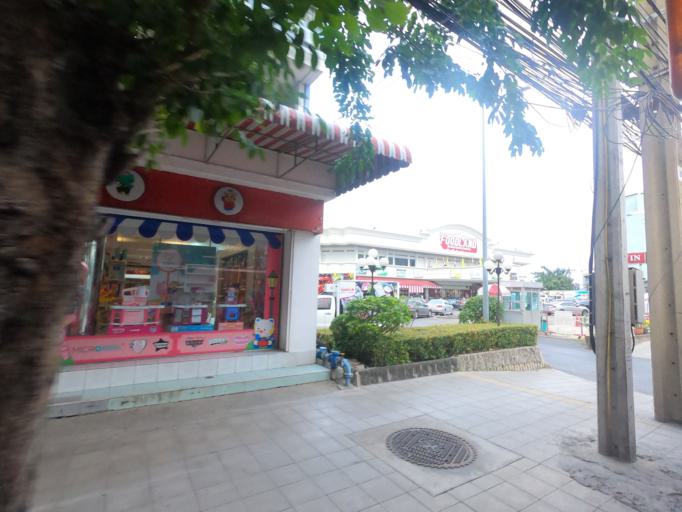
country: TH
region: Bangkok
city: Wang Thonglang
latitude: 13.7791
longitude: 100.6222
